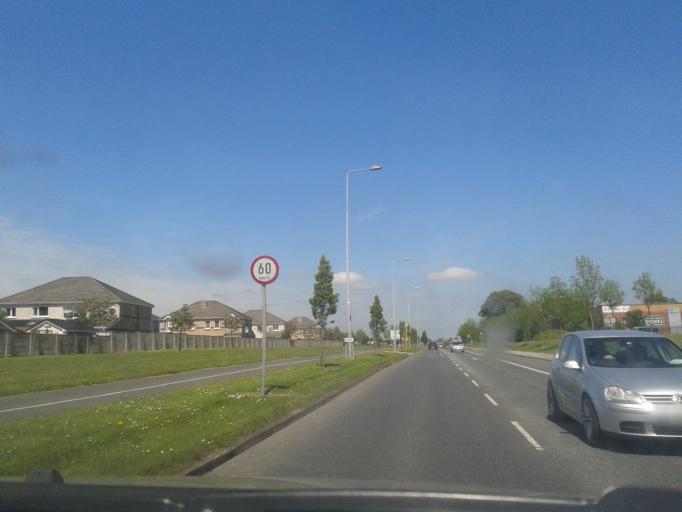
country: IE
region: Leinster
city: Hartstown
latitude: 53.3831
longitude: -6.4033
